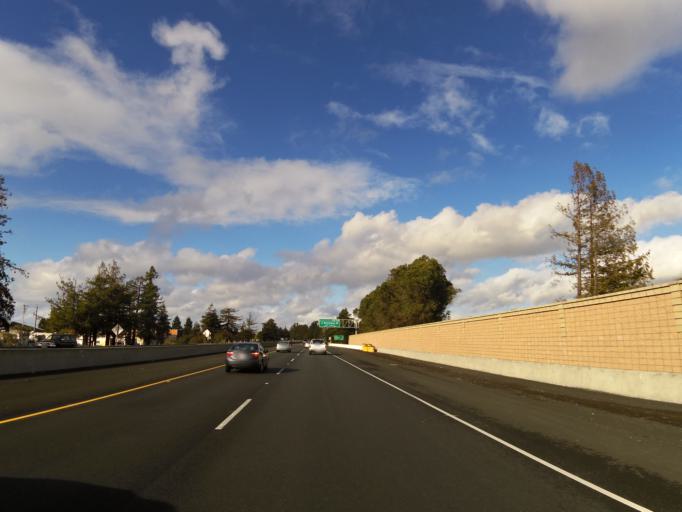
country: US
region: California
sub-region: Sonoma County
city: Petaluma
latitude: 38.2385
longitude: -122.6205
